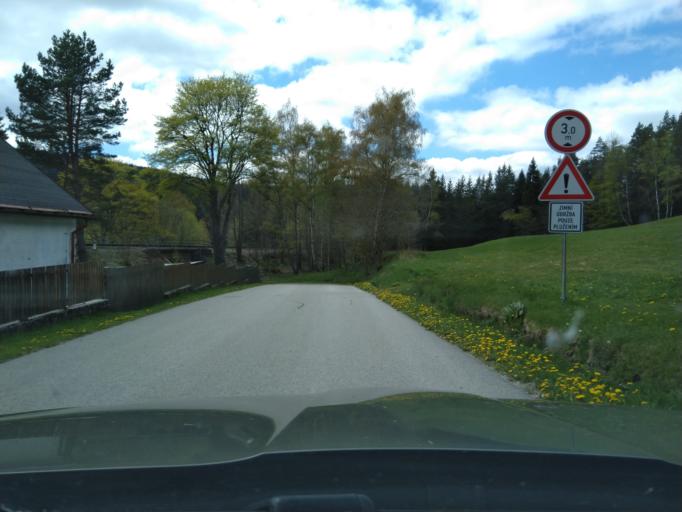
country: CZ
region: Jihocesky
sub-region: Okres Prachatice
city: Vimperk
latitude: 49.0198
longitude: 13.7310
